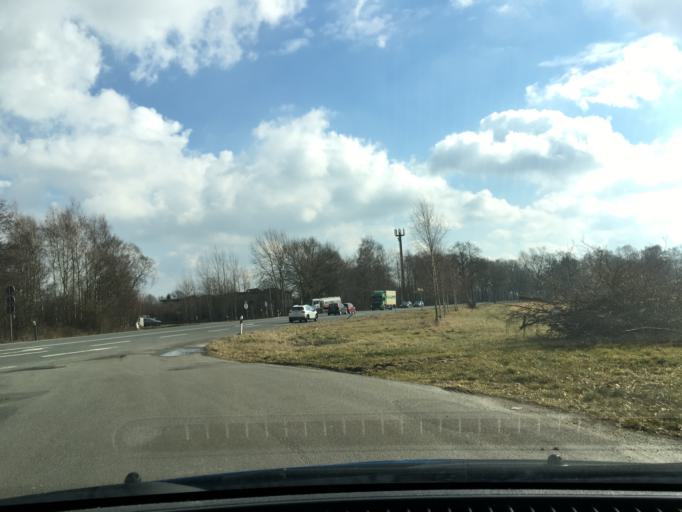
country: DE
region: Lower Saxony
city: Handorf
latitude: 53.3340
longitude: 10.3434
